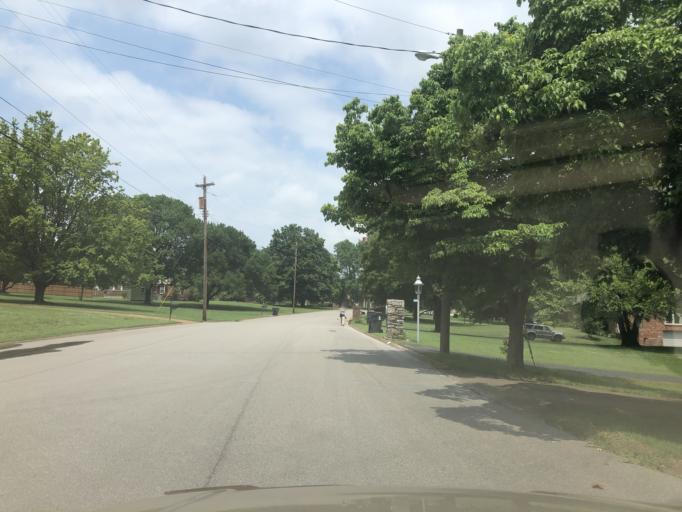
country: US
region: Tennessee
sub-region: Davidson County
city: Lakewood
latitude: 36.2401
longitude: -86.6200
